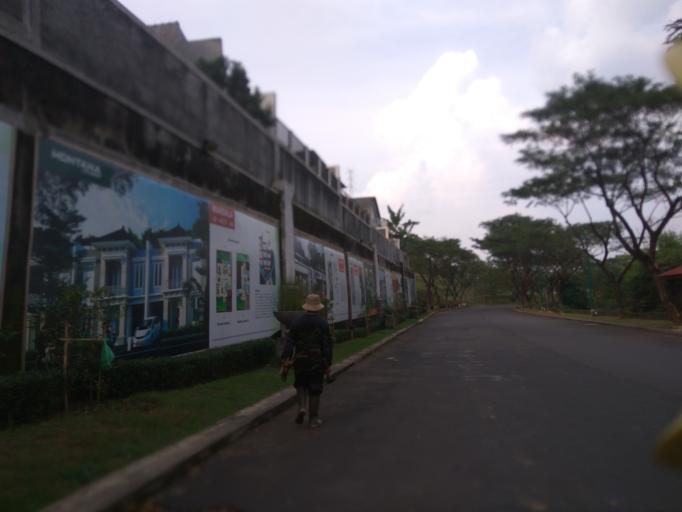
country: ID
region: Central Java
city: Semarang
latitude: -7.0359
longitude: 110.4369
